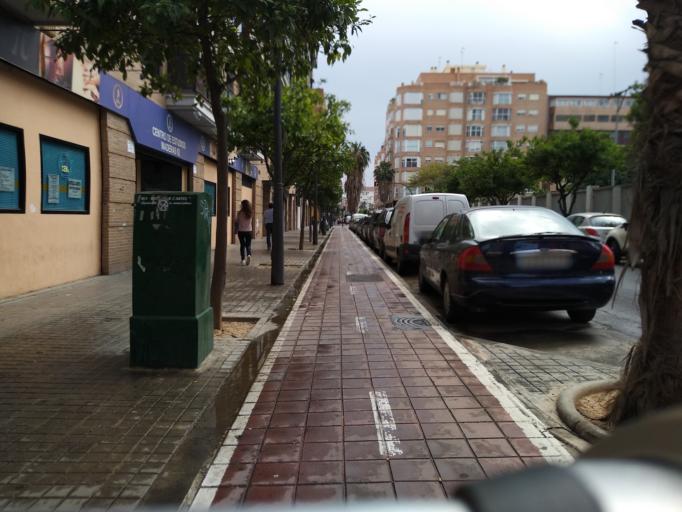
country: ES
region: Valencia
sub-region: Provincia de Valencia
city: Alboraya
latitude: 39.4674
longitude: -0.3370
